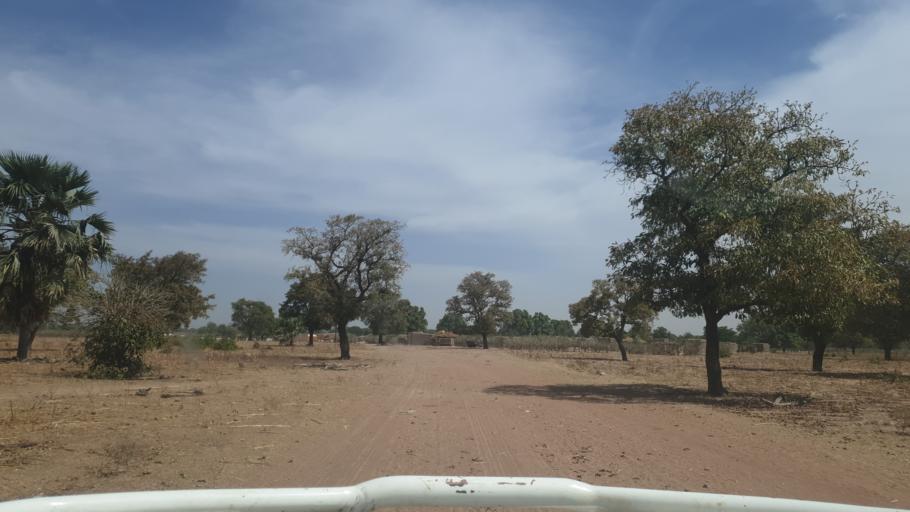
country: ML
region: Sikasso
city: Yorosso
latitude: 12.2759
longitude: -4.6900
